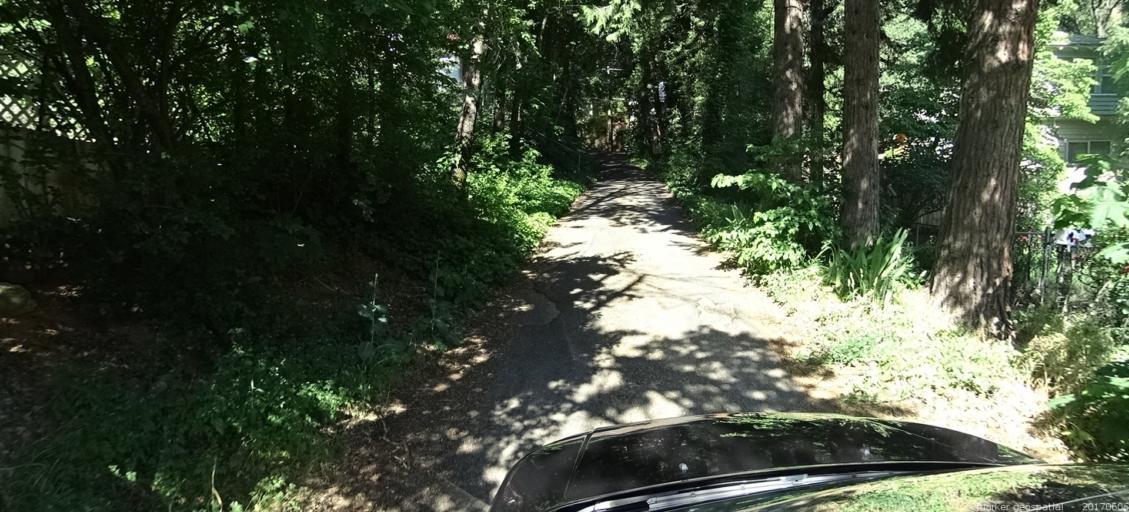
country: US
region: California
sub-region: Siskiyou County
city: Dunsmuir
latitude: 41.2054
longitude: -122.2752
